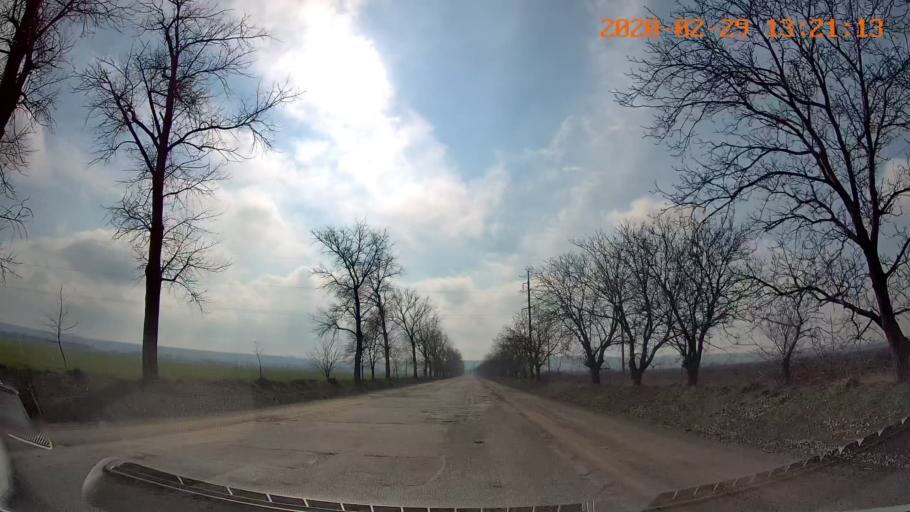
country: MD
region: Telenesti
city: Camenca
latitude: 47.9722
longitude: 28.6349
